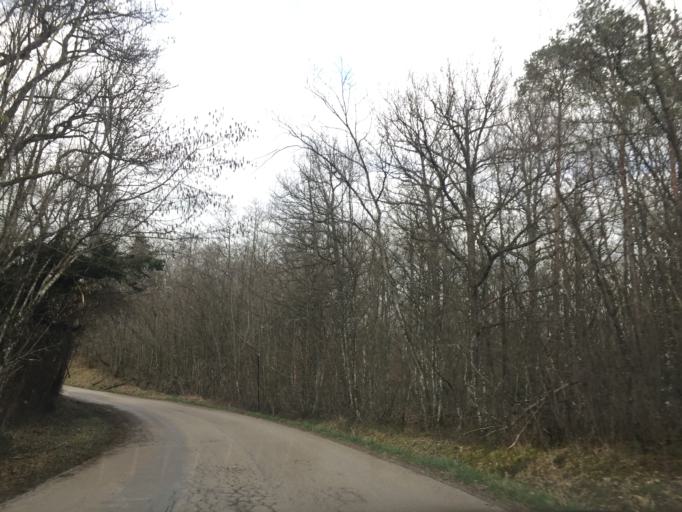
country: BE
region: Wallonia
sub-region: Province du Luxembourg
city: Durbuy
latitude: 50.3214
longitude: 5.4887
